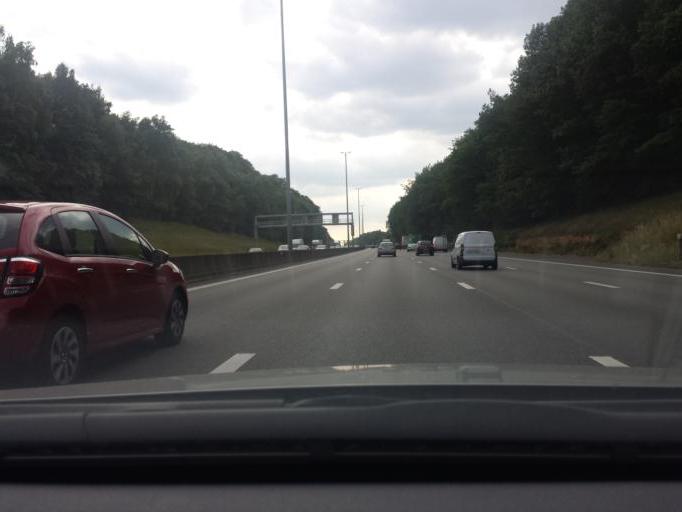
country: BE
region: Flanders
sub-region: Provincie Vlaams-Brabant
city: Kortenberg
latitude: 50.8689
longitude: 4.5574
